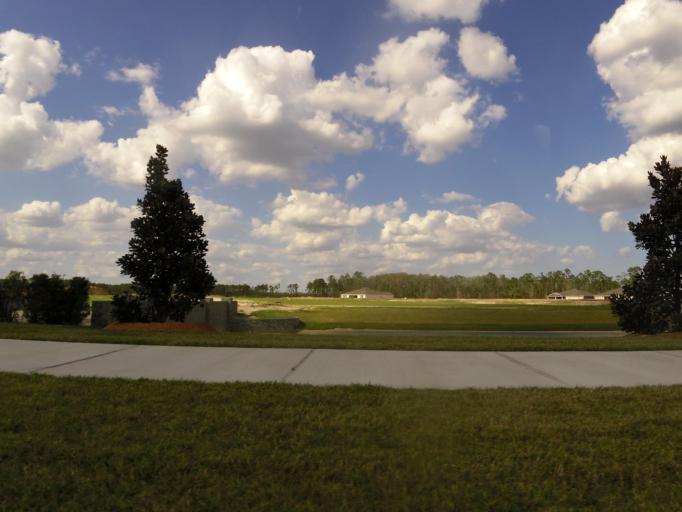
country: US
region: Florida
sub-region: Saint Johns County
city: Palm Valley
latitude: 30.1741
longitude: -81.5081
